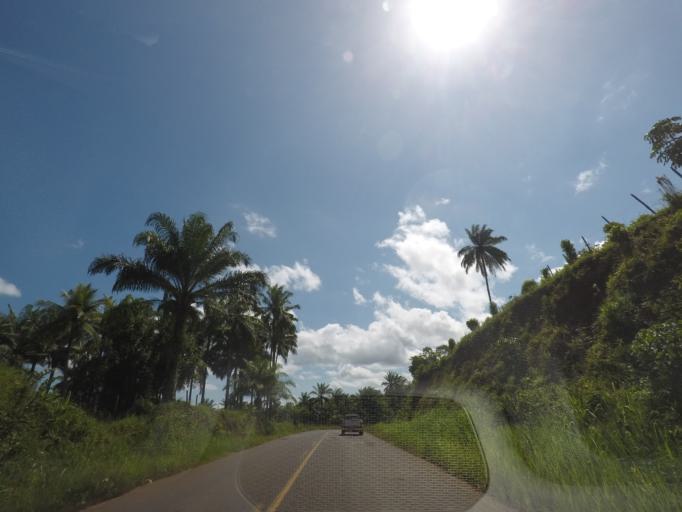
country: BR
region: Bahia
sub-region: Taperoa
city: Taperoa
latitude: -13.5533
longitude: -39.1022
